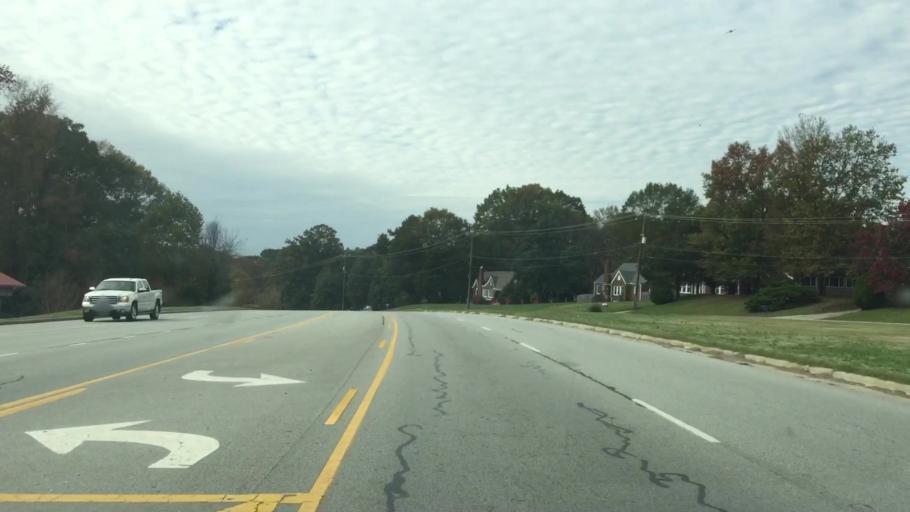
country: US
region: North Carolina
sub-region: Rowan County
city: Salisbury
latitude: 35.6636
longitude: -80.5051
